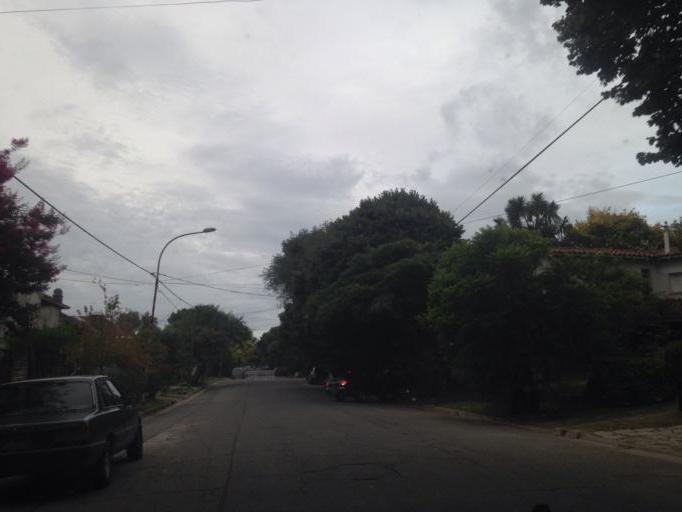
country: AR
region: Buenos Aires
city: Mar del Plata
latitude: -38.0231
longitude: -57.5377
